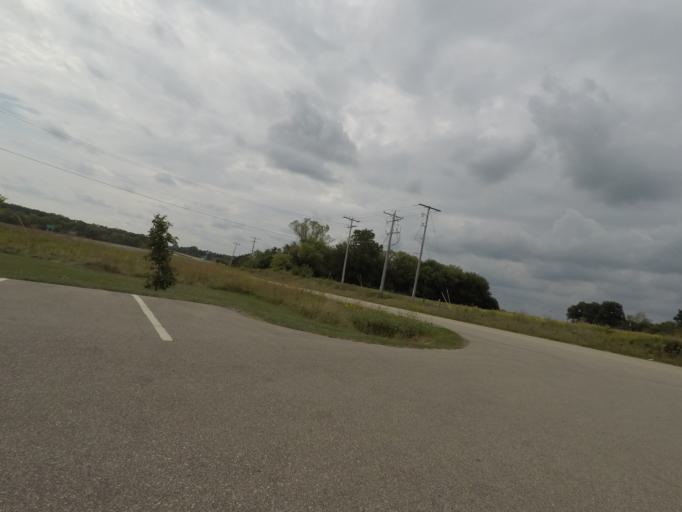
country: US
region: Wisconsin
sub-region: Jefferson County
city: Lake Koshkonong
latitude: 42.8471
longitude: -88.9192
